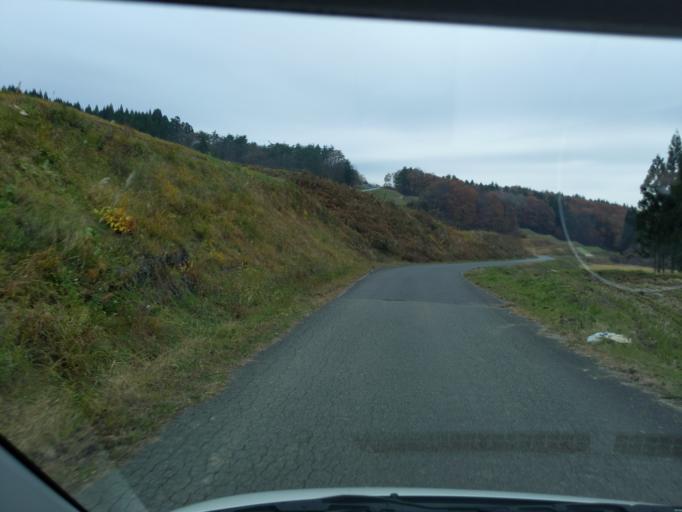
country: JP
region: Iwate
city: Ichinoseki
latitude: 39.0011
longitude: 141.0272
